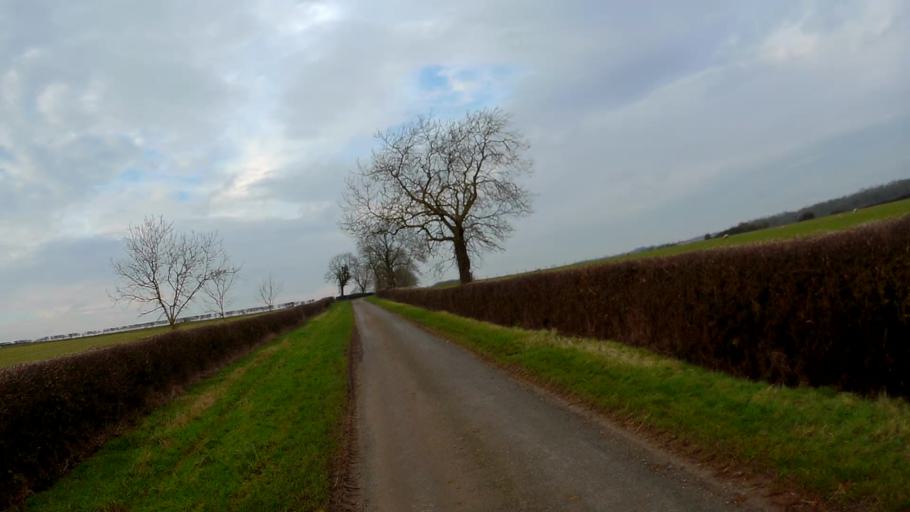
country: GB
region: England
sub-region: Lincolnshire
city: Bourne
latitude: 52.8207
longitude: -0.4561
